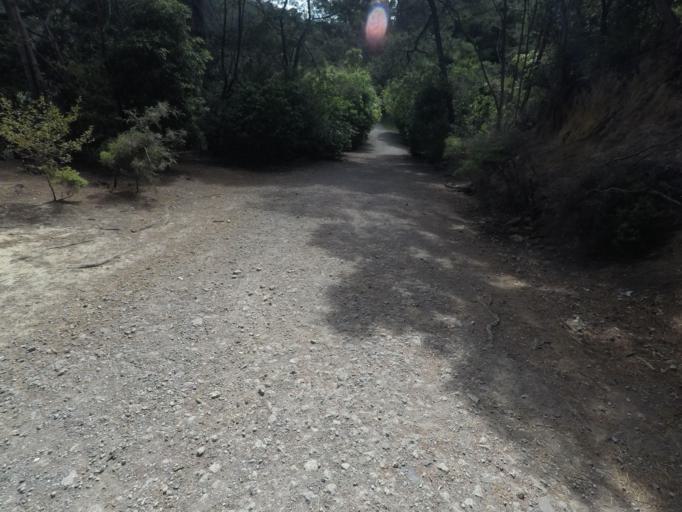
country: NZ
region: Auckland
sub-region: Auckland
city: North Shore
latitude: -36.8141
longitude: 174.6974
